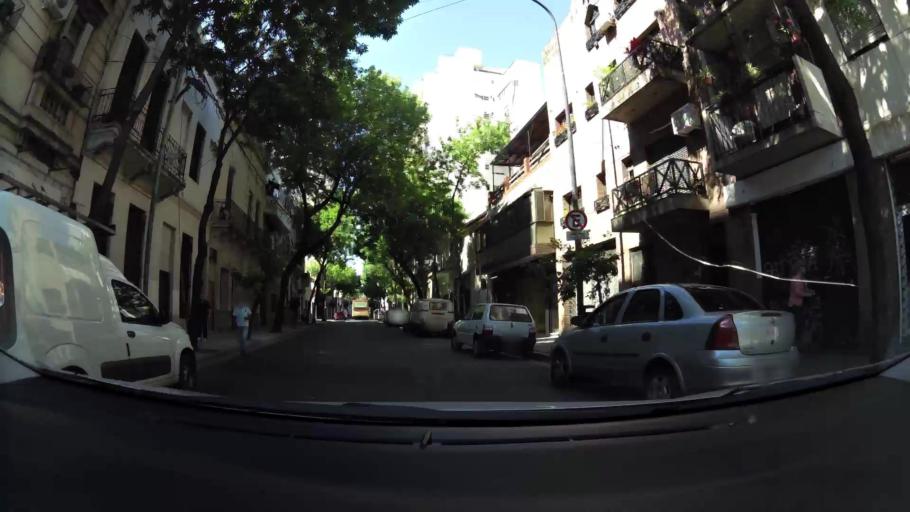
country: AR
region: Buenos Aires F.D.
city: Buenos Aires
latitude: -34.6211
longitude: -58.3844
